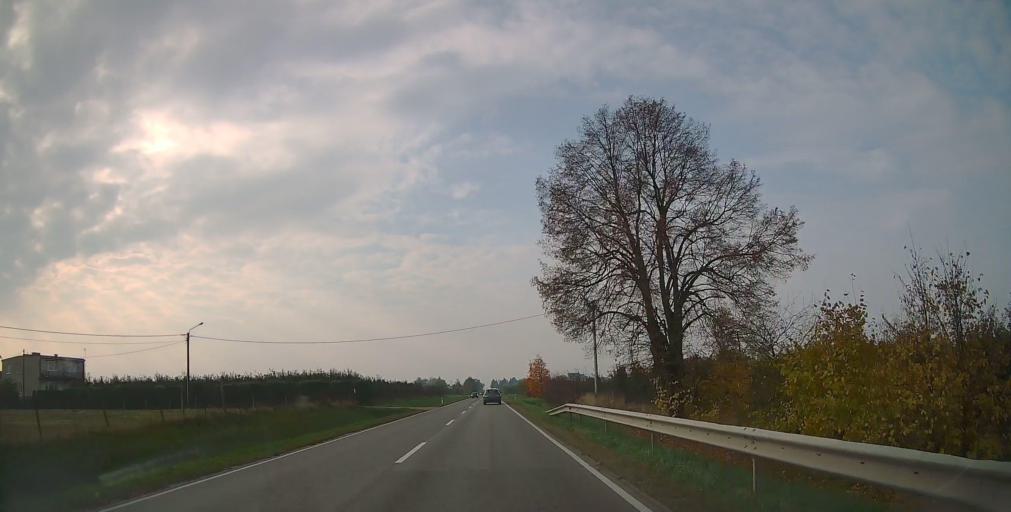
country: PL
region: Masovian Voivodeship
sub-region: Powiat grojecki
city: Belsk Duzy
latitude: 51.7836
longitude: 20.7765
